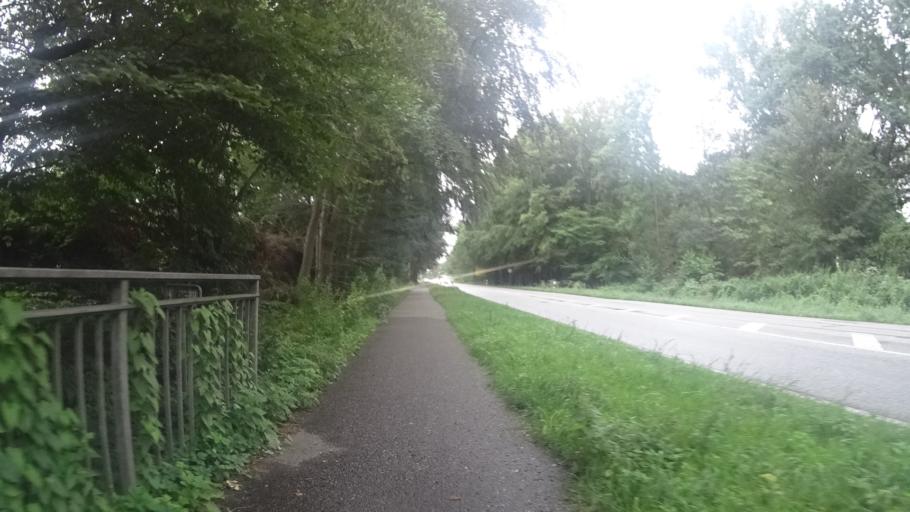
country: DE
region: Schleswig-Holstein
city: Kolln-Reisiek
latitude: 53.7589
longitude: 9.6830
